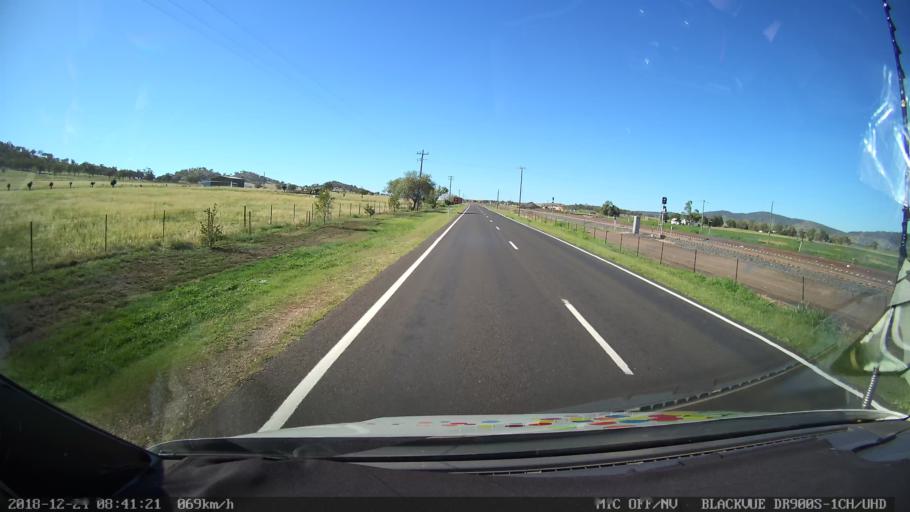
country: AU
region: New South Wales
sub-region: Liverpool Plains
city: Quirindi
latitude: -31.3624
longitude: 150.6451
